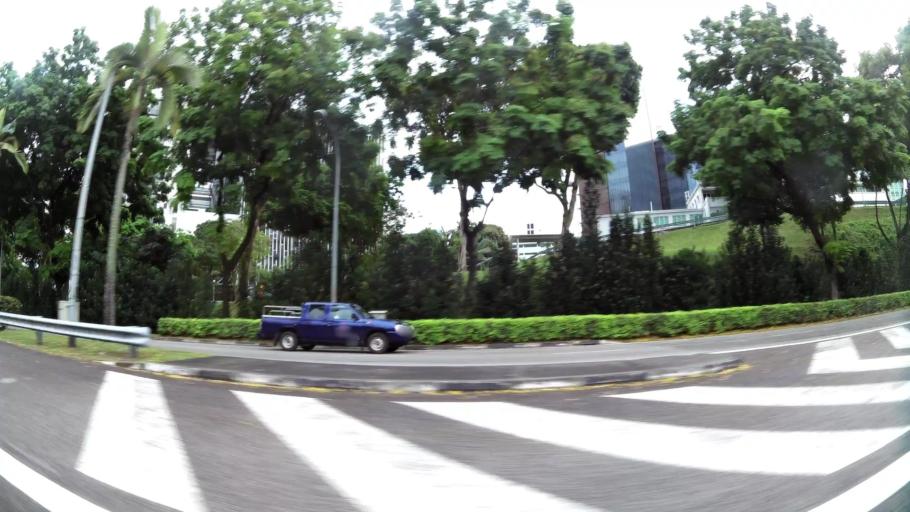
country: SG
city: Singapore
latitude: 1.2825
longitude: 103.8342
